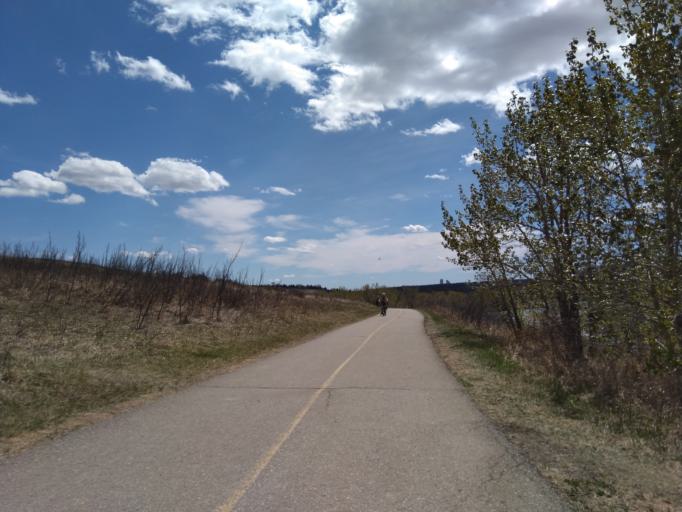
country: CA
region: Alberta
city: Calgary
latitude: 51.0948
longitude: -114.1846
